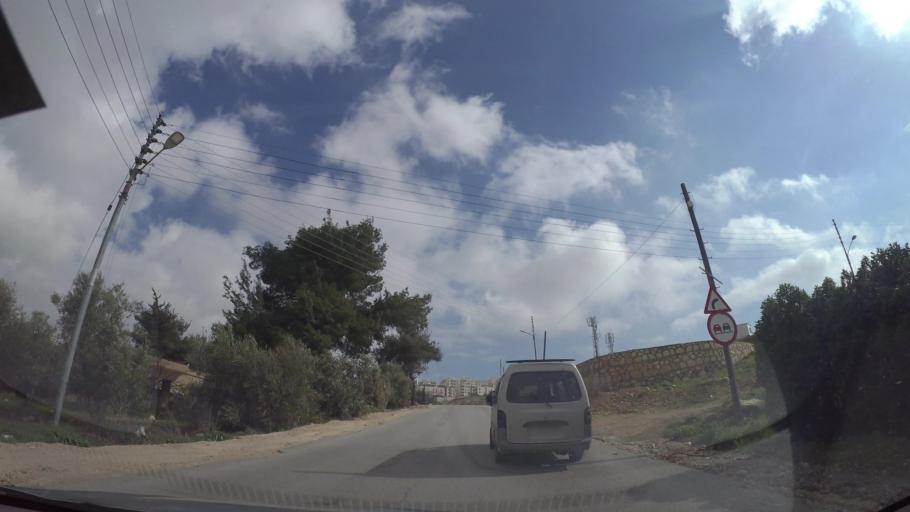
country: JO
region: Amman
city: Al Jubayhah
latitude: 32.0685
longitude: 35.8691
